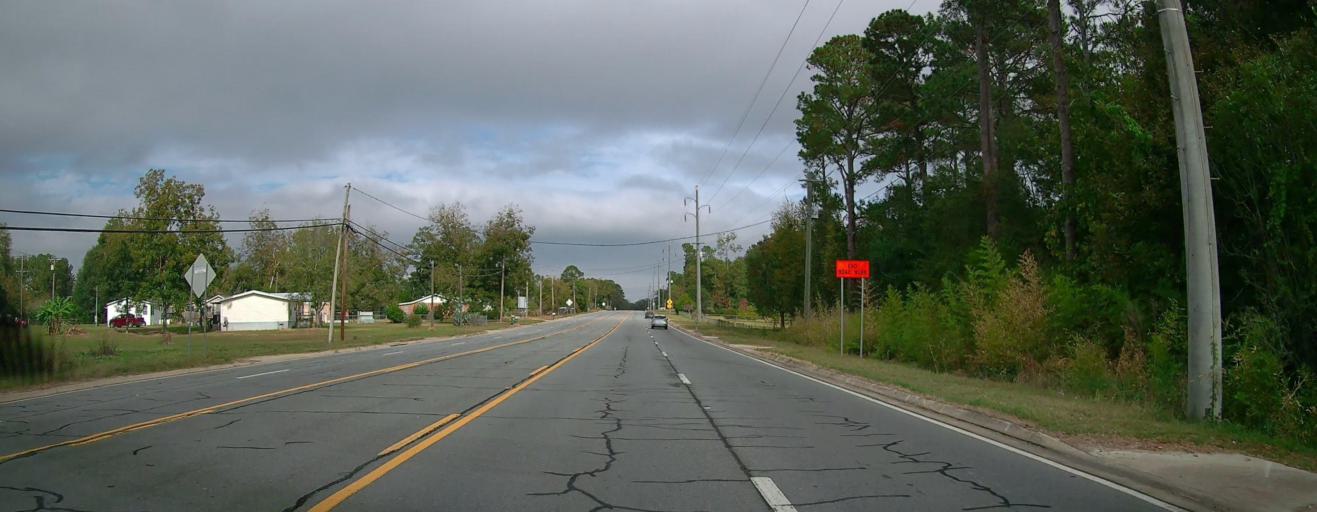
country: US
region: Georgia
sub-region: Colquitt County
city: Moultrie
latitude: 31.2106
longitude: -83.7765
